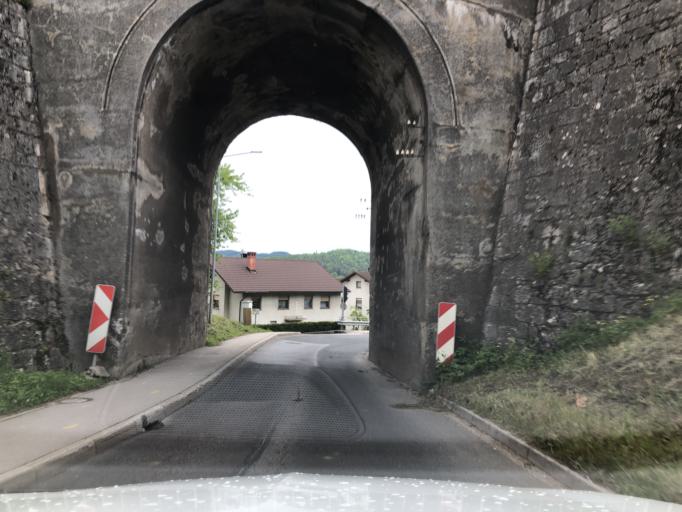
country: SI
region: Cerknica
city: Rakek
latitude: 45.8132
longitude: 14.3153
